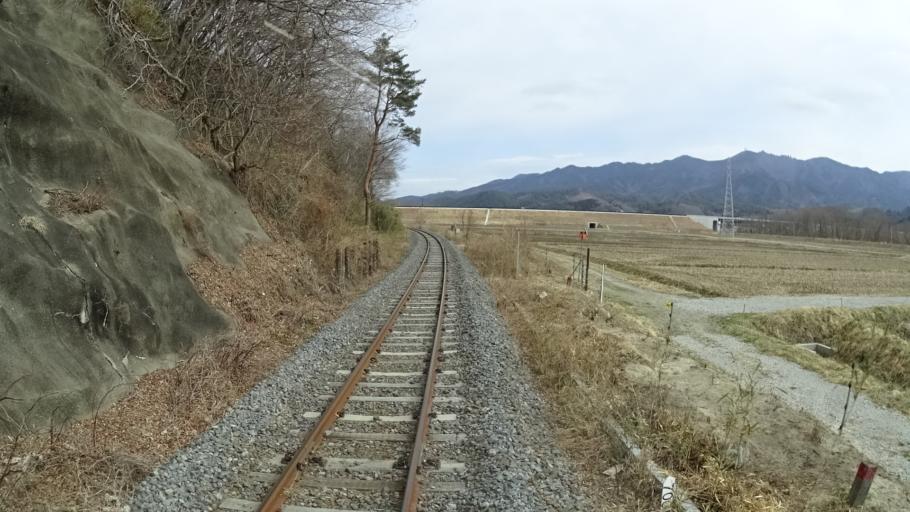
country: JP
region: Iwate
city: Yamada
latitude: 39.5245
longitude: 141.9197
